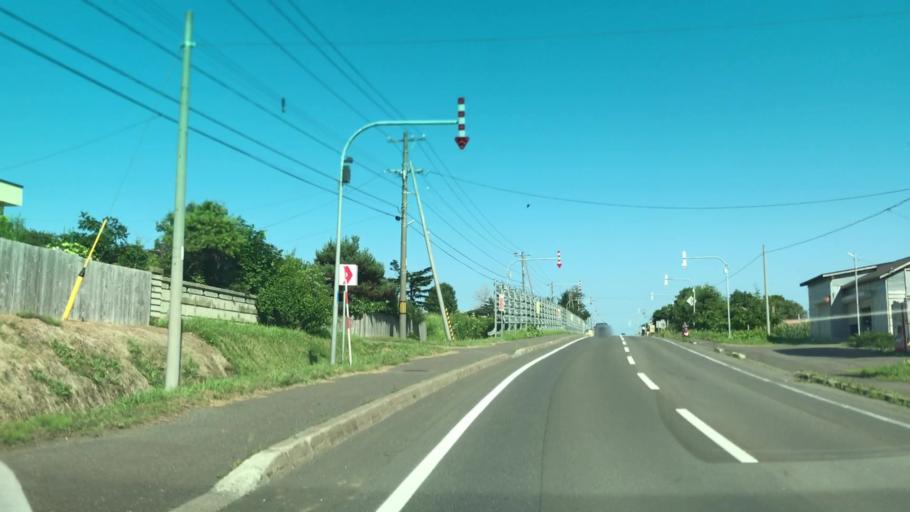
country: JP
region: Hokkaido
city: Iwanai
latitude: 42.9843
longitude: 140.5599
